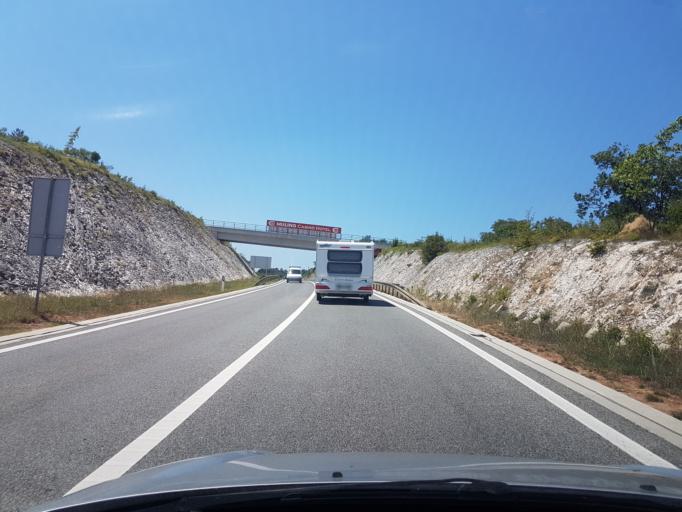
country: SI
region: Piran-Pirano
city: Seca
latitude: 45.4551
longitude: 13.6270
